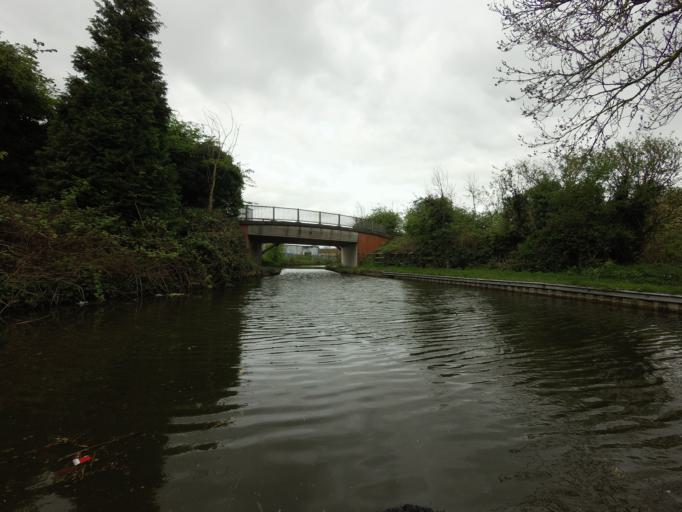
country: GB
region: England
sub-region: Milton Keynes
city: Water Eaton
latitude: 52.0037
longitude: -0.7162
